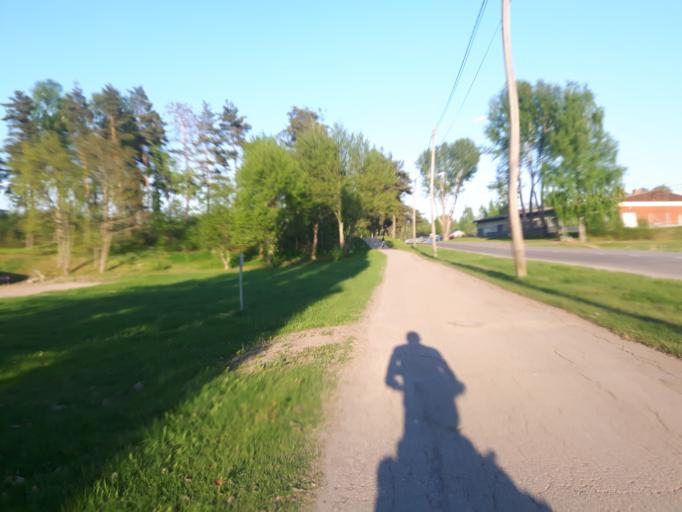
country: FI
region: Uusimaa
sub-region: Loviisa
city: Lovisa
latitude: 60.4572
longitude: 26.2017
